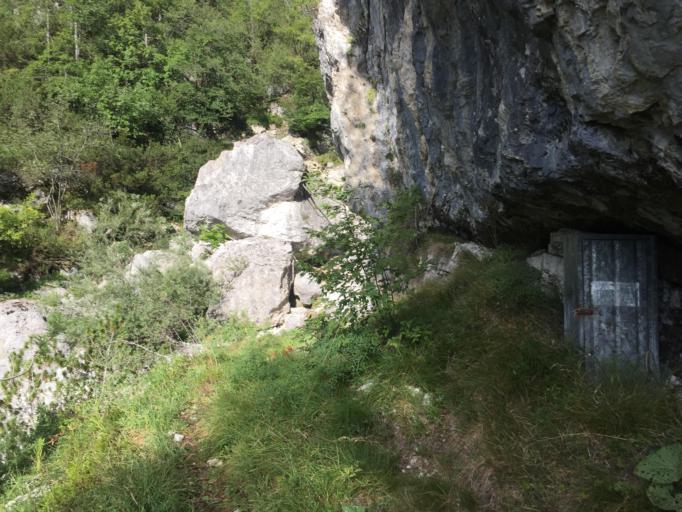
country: IT
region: Friuli Venezia Giulia
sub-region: Provincia di Udine
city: Chiusaforte
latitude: 46.4319
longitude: 13.2858
